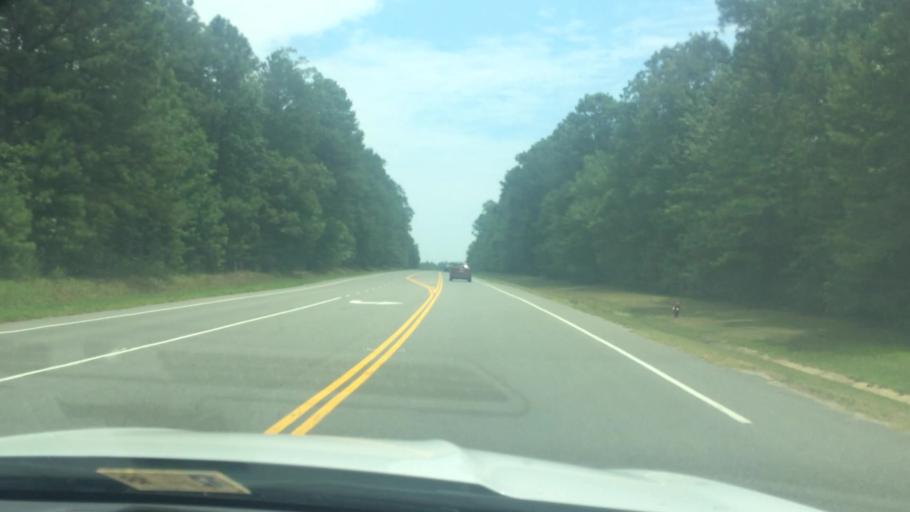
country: US
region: Virginia
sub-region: James City County
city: Williamsburg
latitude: 37.2639
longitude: -76.7966
